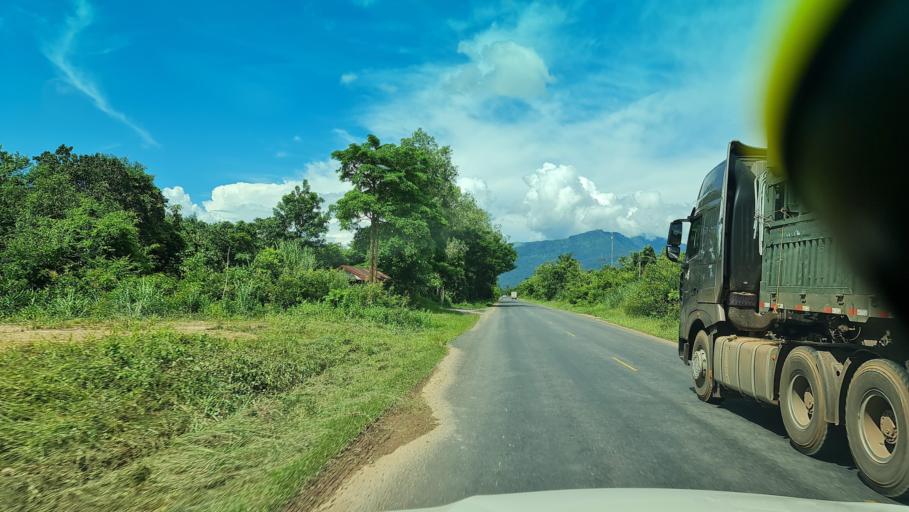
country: LA
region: Bolikhamxai
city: Pakkading
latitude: 18.2929
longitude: 104.0834
